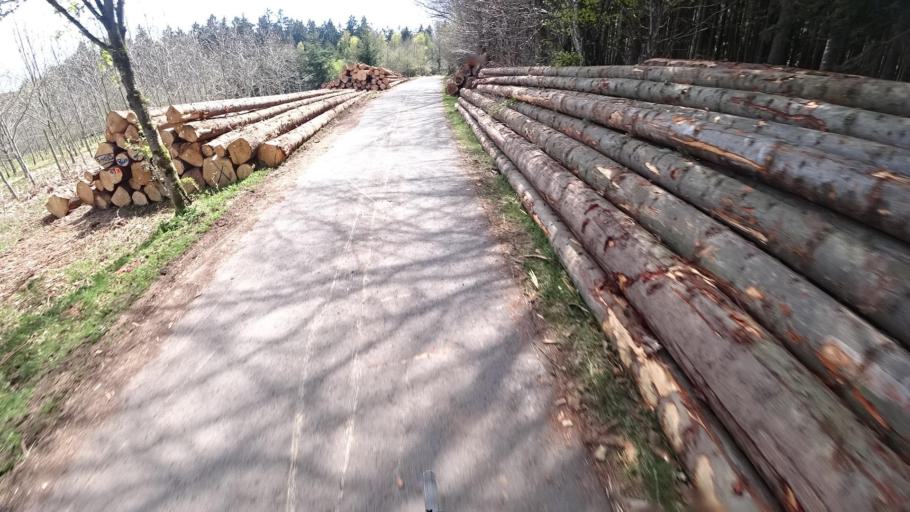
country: DE
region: Rheinland-Pfalz
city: Gusenburg
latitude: 49.6379
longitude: 6.8872
